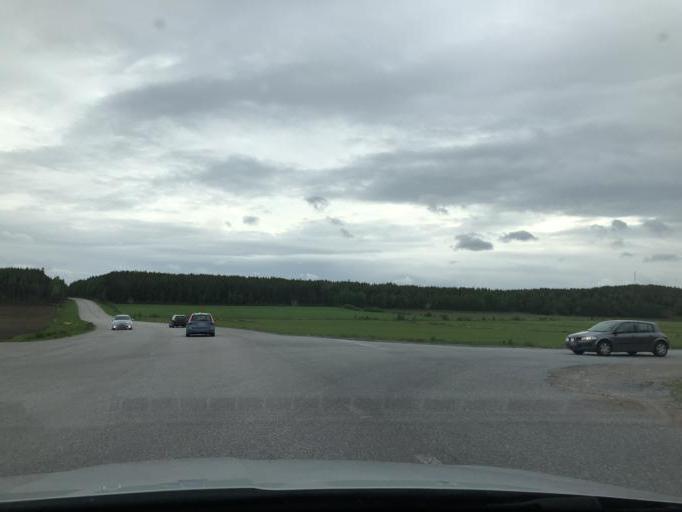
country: SE
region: Norrbotten
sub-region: Pitea Kommun
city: Norrfjarden
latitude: 65.3722
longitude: 21.4217
